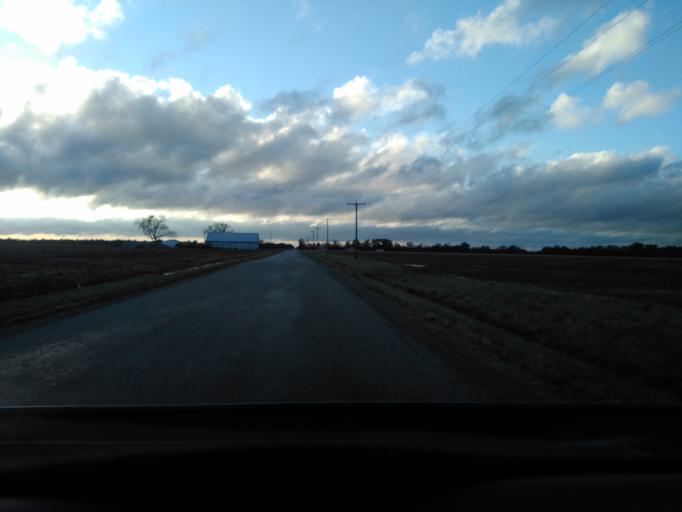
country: US
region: Illinois
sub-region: Effingham County
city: Altamont
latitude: 38.9574
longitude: -88.7393
